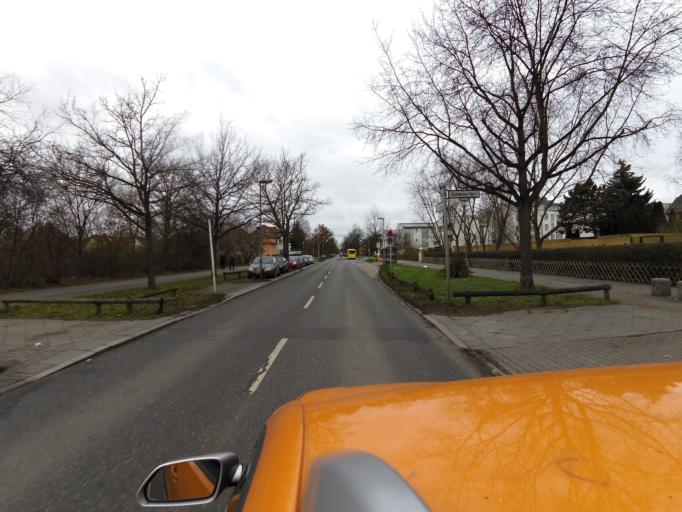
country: DE
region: Berlin
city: Mariendorf
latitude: 52.4395
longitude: 13.4042
